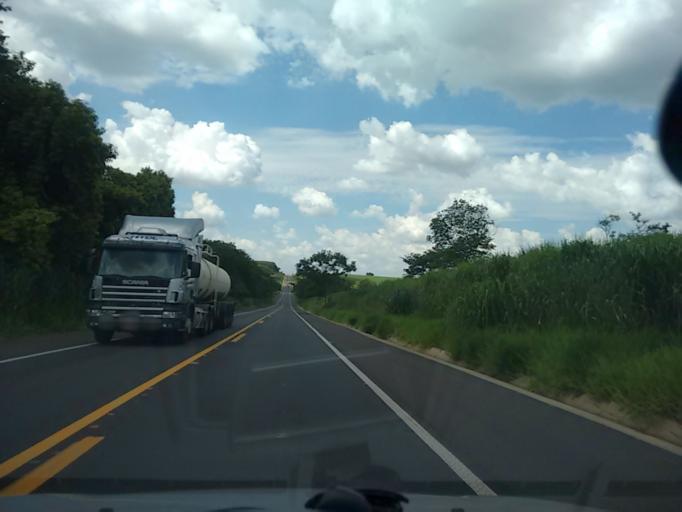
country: BR
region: Sao Paulo
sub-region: Osvaldo Cruz
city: Osvaldo Cruz
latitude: -21.8433
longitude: -50.8303
